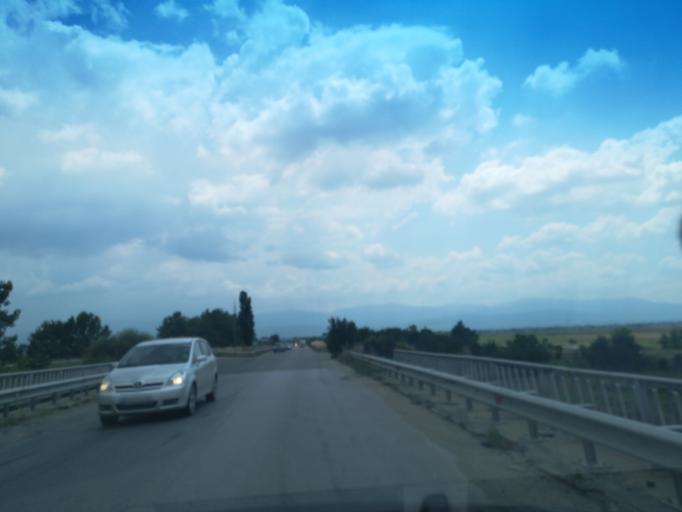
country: BG
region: Plovdiv
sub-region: Obshtina Plovdiv
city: Plovdiv
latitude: 42.1907
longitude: 24.6765
